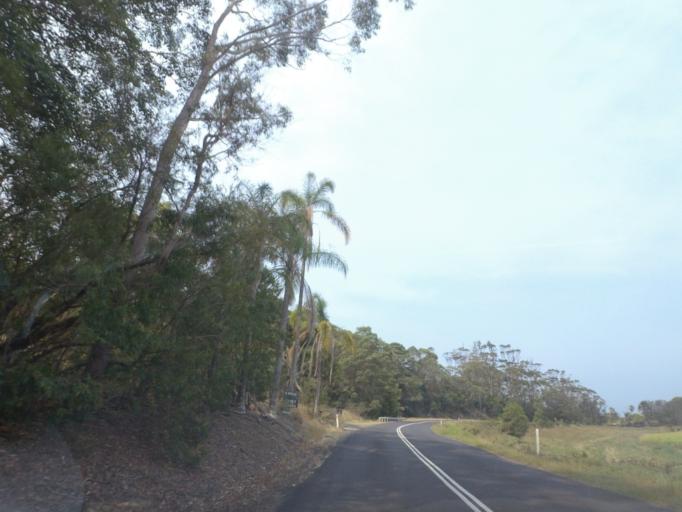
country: AU
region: New South Wales
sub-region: Tweed
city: Burringbar
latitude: -28.4536
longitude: 153.5316
